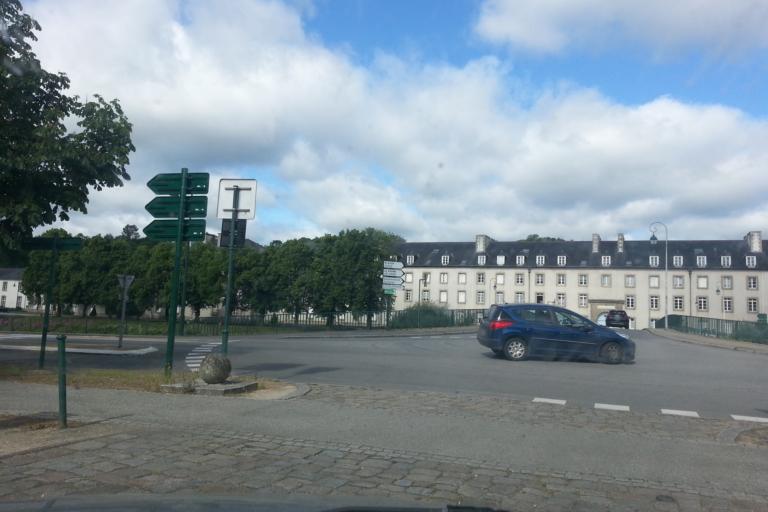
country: FR
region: Brittany
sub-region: Departement du Morbihan
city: Pontivy
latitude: 48.0656
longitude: -2.9683
